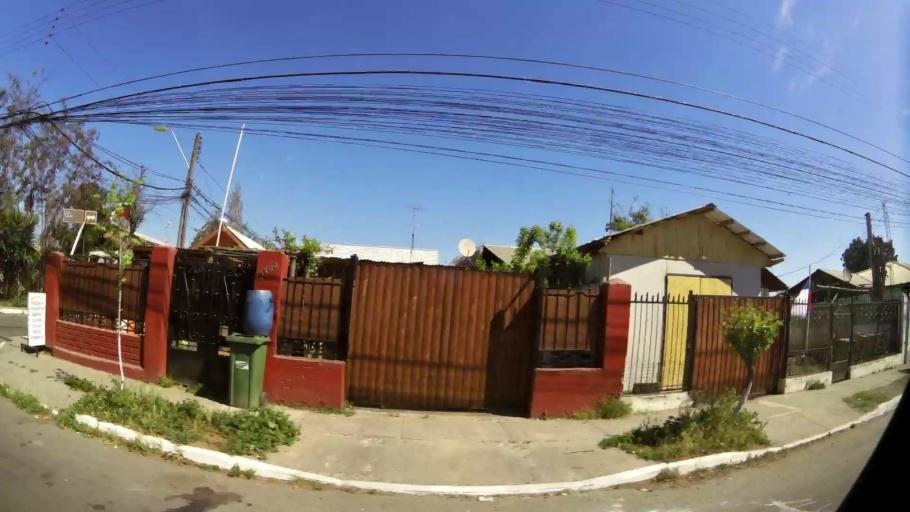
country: CL
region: Santiago Metropolitan
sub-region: Provincia de Talagante
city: Penaflor
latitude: -33.6016
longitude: -70.8787
